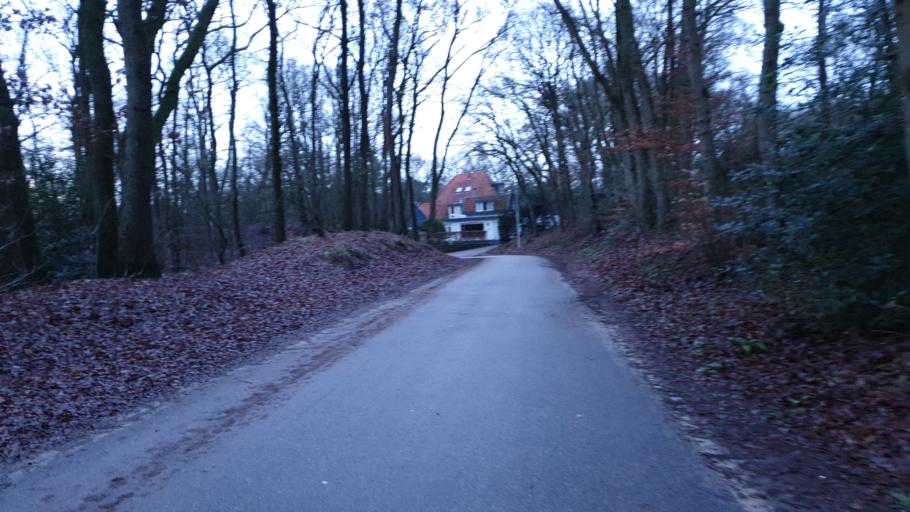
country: NL
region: Gelderland
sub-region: Gemeente Ede
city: Otterlo
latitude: 52.0998
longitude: 5.7788
